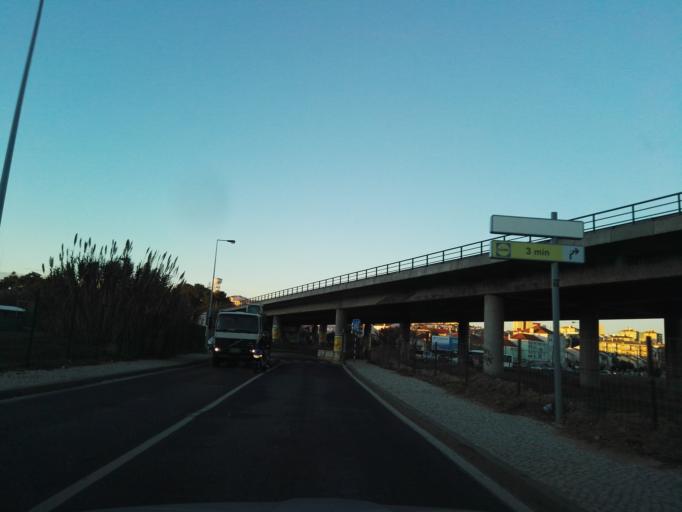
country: PT
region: Setubal
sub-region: Seixal
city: Corroios
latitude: 38.6412
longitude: -9.1488
